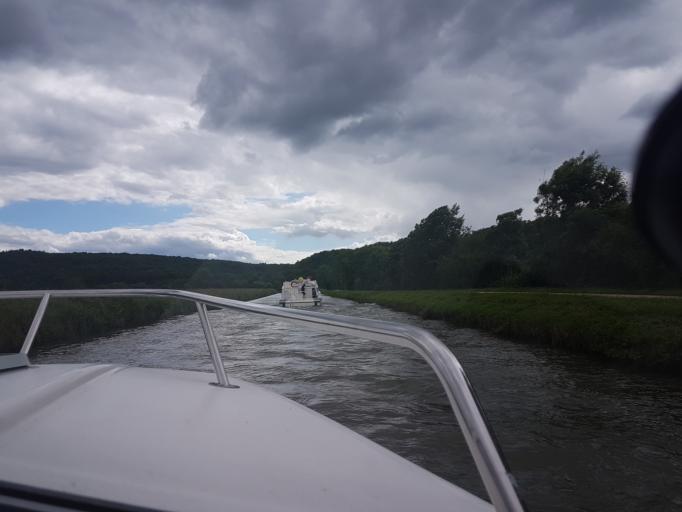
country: FR
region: Bourgogne
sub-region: Departement de l'Yonne
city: Vermenton
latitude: 47.5715
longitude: 3.6403
